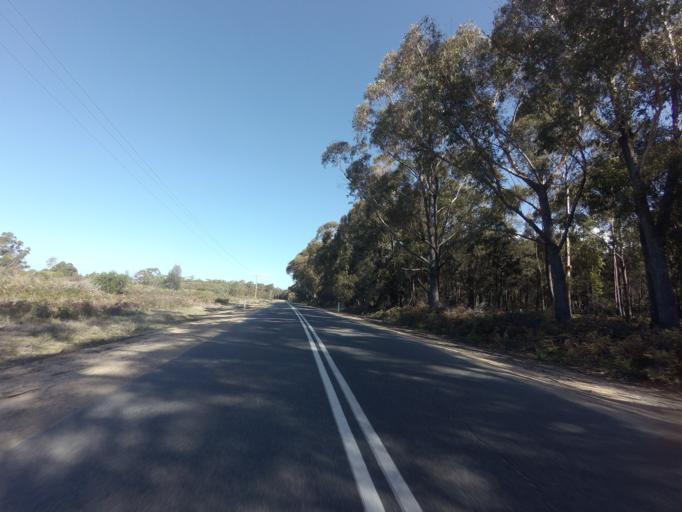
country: AU
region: Tasmania
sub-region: Break O'Day
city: St Helens
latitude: -41.6767
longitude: 148.2779
